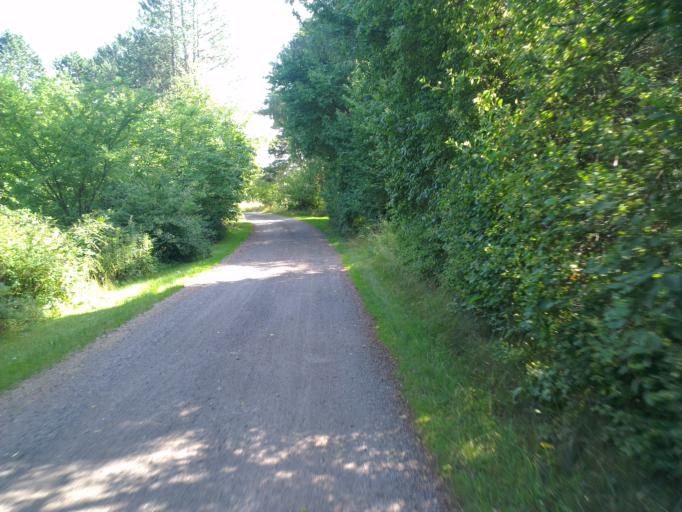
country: DK
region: Capital Region
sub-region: Halsnaes Kommune
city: Hundested
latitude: 55.9255
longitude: 11.9307
